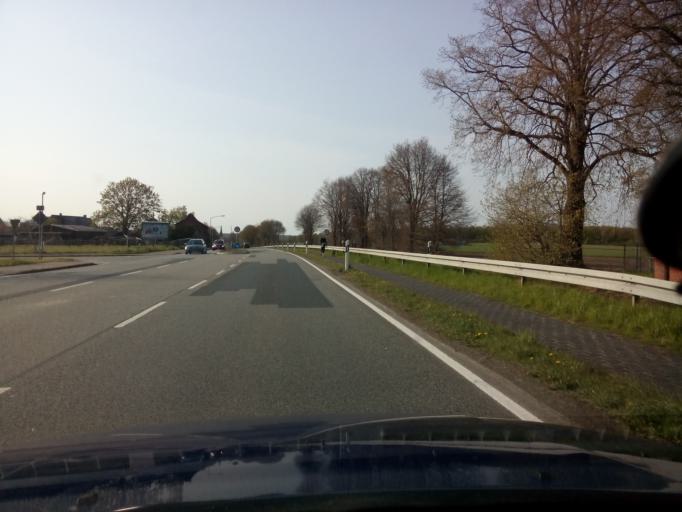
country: DE
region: Lower Saxony
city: Syke
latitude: 52.9035
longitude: 8.8406
